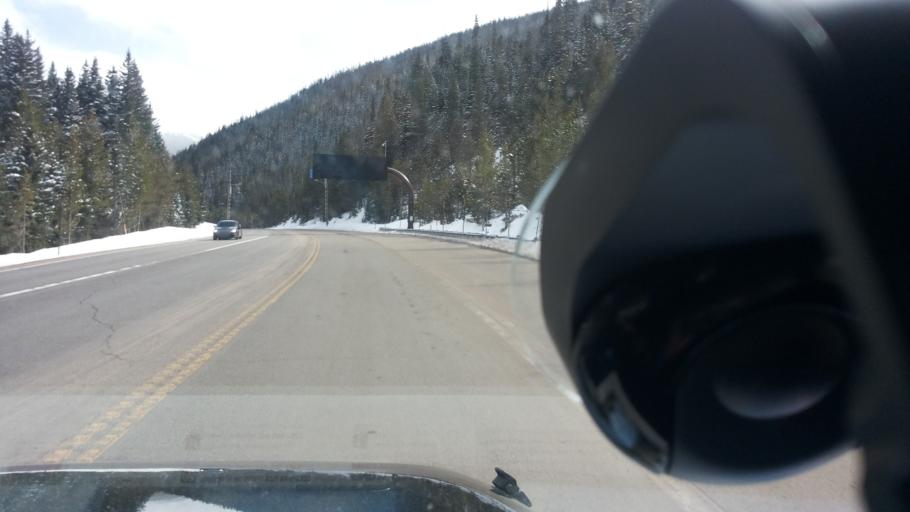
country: US
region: Colorado
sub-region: Grand County
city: Fraser
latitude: 39.8578
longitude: -105.7522
